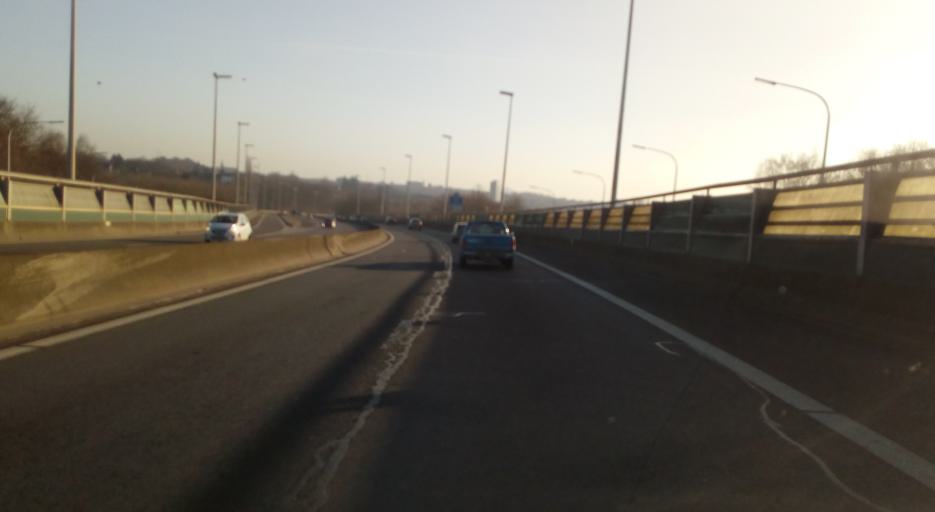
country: BE
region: Wallonia
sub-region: Province du Hainaut
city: Charleroi
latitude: 50.4386
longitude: 4.4441
